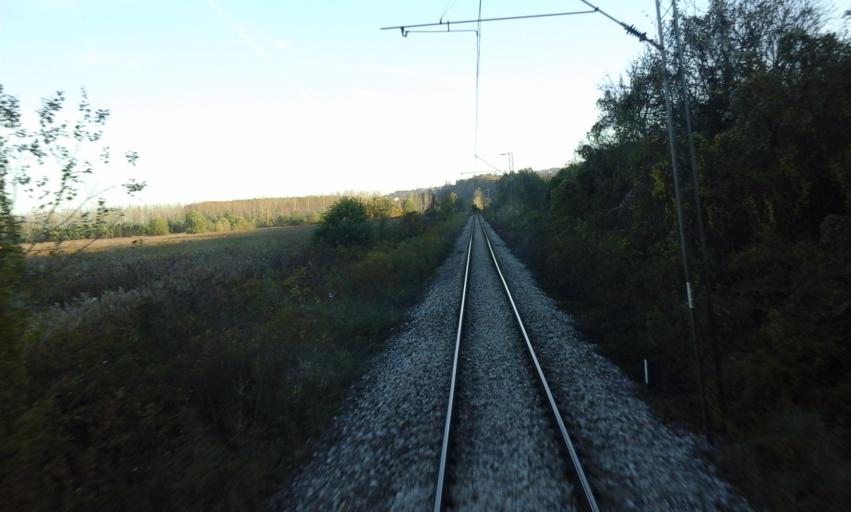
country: RS
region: Autonomna Pokrajina Vojvodina
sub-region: Juznobacki Okrug
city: Sremski Karlovci
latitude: 45.2205
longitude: 19.9067
